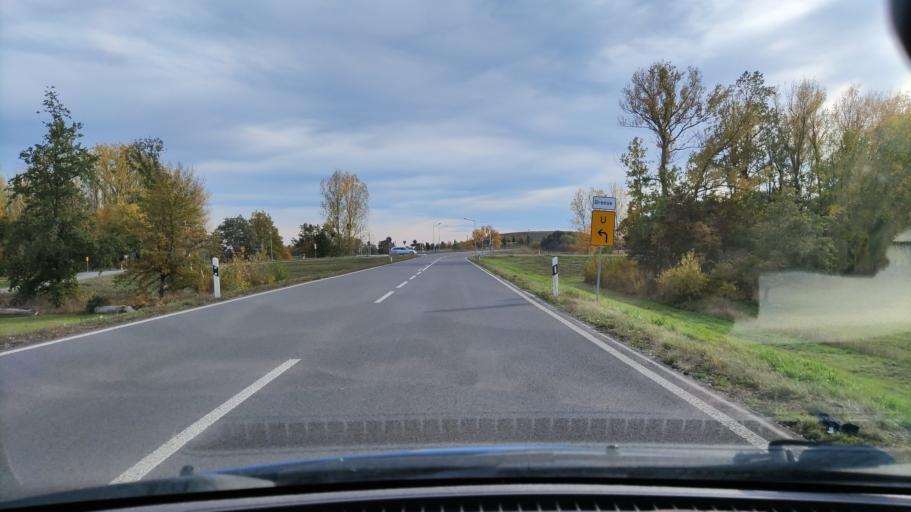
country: DE
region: Brandenburg
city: Breese
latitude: 52.9998
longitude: 11.7824
